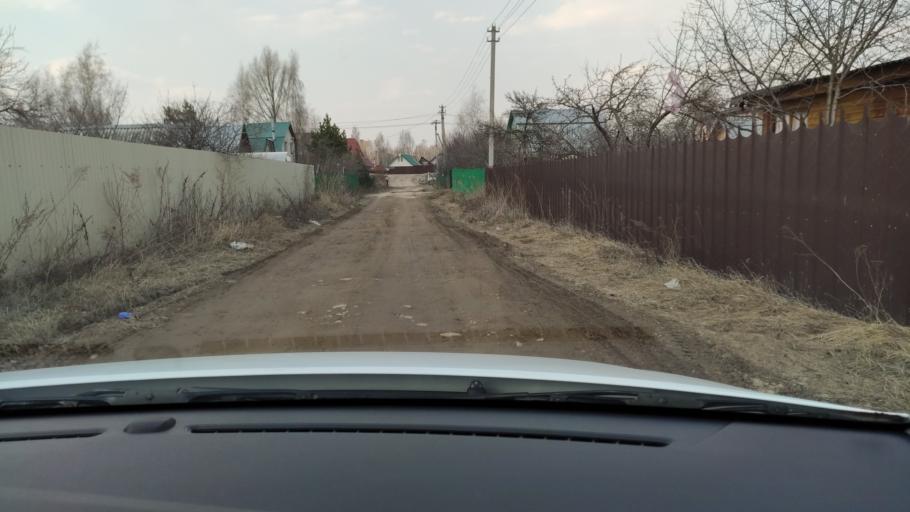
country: RU
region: Tatarstan
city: Stolbishchi
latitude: 55.6933
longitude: 49.2017
